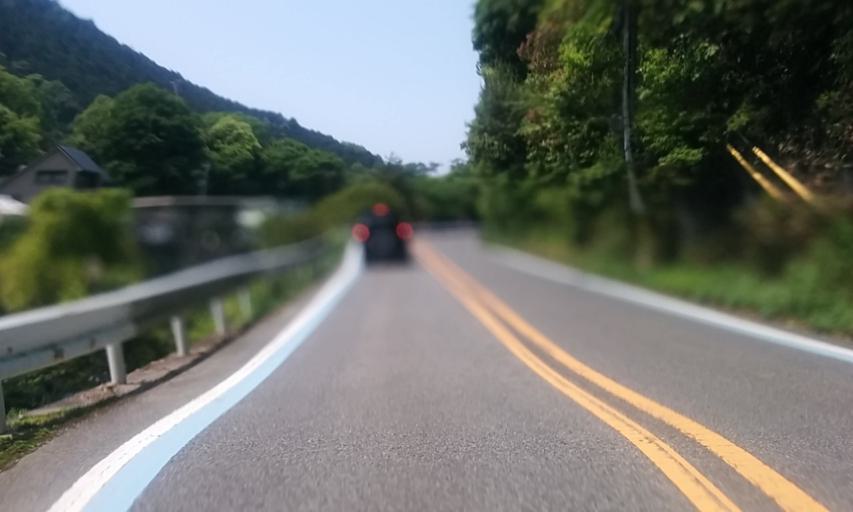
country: JP
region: Ehime
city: Niihama
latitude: 33.9182
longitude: 133.3119
